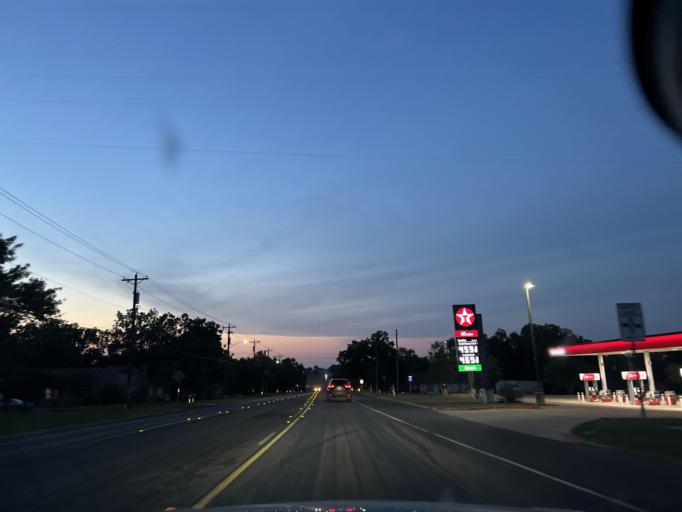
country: US
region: Texas
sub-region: Washington County
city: Brenham
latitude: 30.1821
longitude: -96.4023
